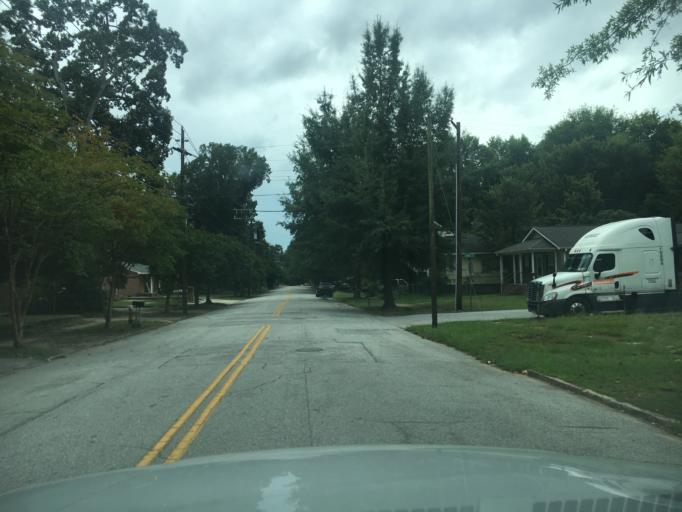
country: US
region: South Carolina
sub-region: Greenville County
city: Greenville
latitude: 34.8610
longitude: -82.4115
